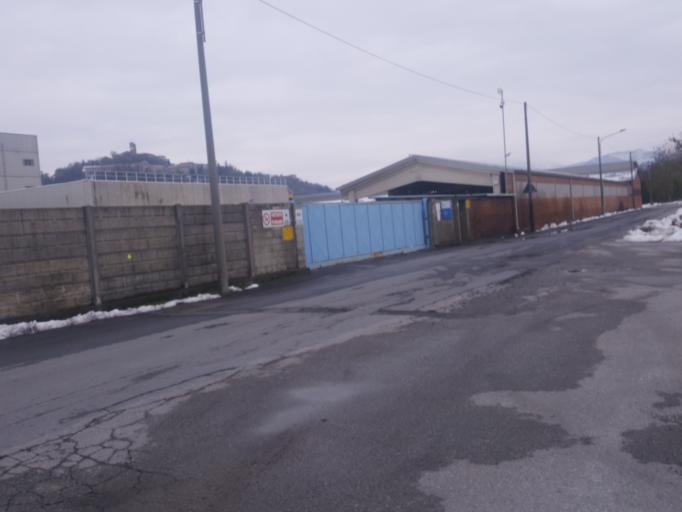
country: IT
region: Piedmont
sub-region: Provincia di Cuneo
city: Breo
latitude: 44.4015
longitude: 7.8235
